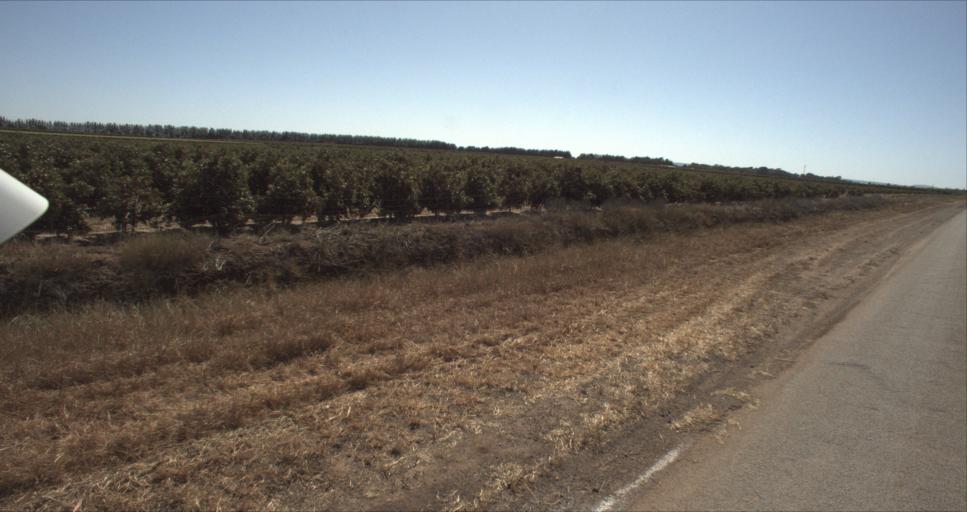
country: AU
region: New South Wales
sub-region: Leeton
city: Leeton
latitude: -34.5330
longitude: 146.3183
